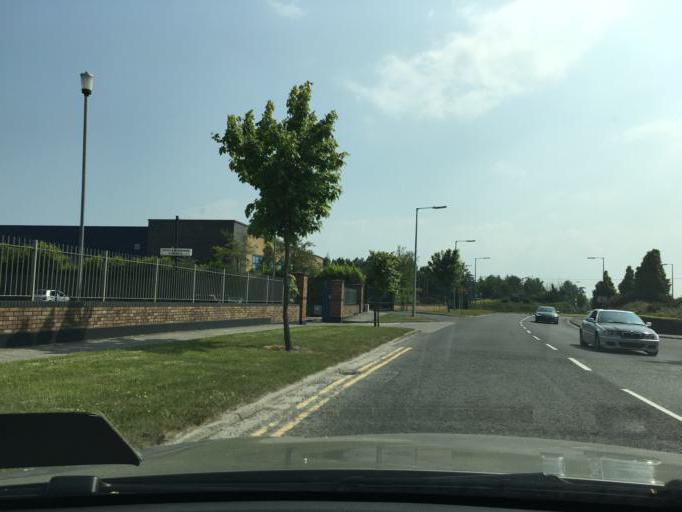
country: IE
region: Leinster
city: Hartstown
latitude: 53.4102
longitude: -6.4092
